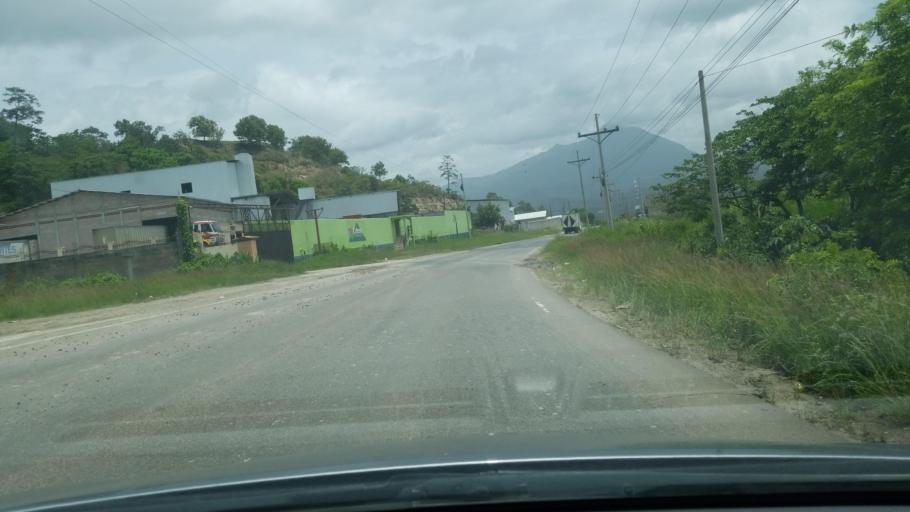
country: HN
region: Copan
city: Cucuyagua
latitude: 14.6693
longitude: -88.8574
